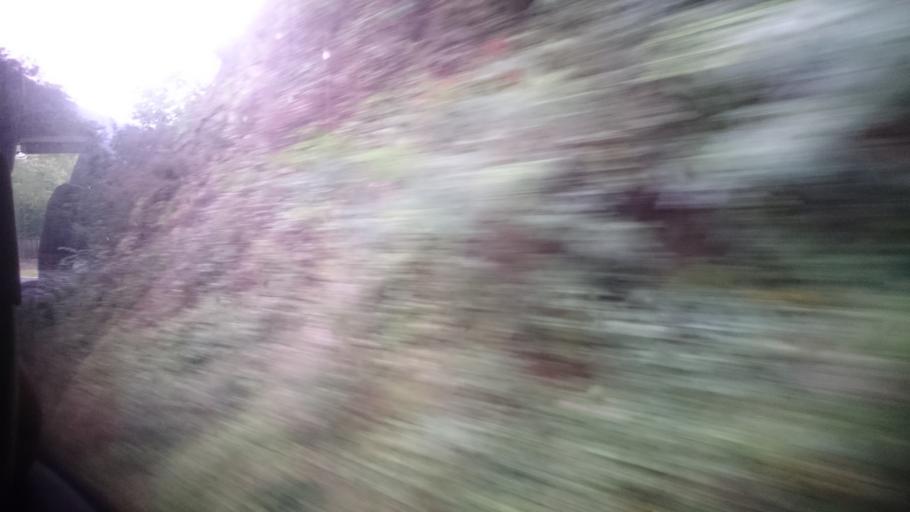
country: ES
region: Asturias
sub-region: Province of Asturias
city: Amieva
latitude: 43.3104
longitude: -5.0526
